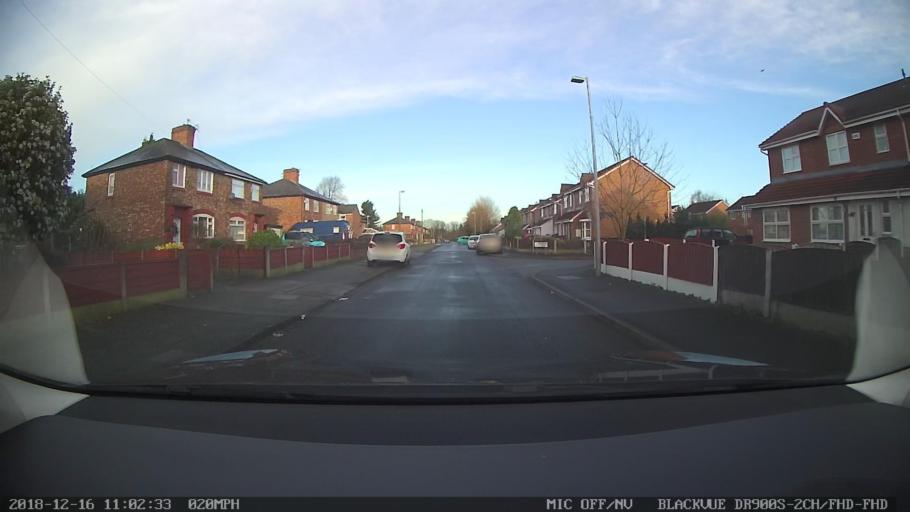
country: GB
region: England
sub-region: Manchester
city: Swinton
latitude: 53.4795
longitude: -2.3701
